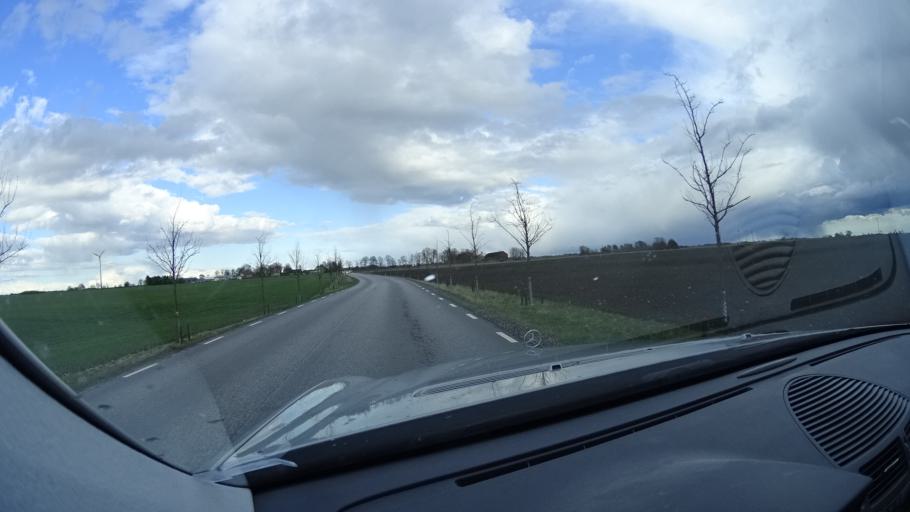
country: SE
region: Skane
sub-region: Eslovs Kommun
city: Eslov
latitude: 55.8073
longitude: 13.3378
